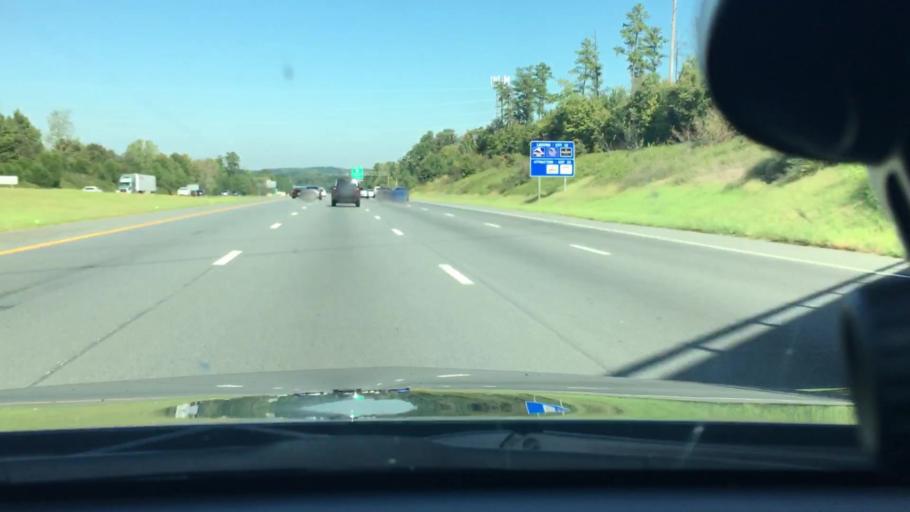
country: US
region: North Carolina
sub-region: Cabarrus County
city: Harrisburg
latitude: 35.3201
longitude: -80.7125
